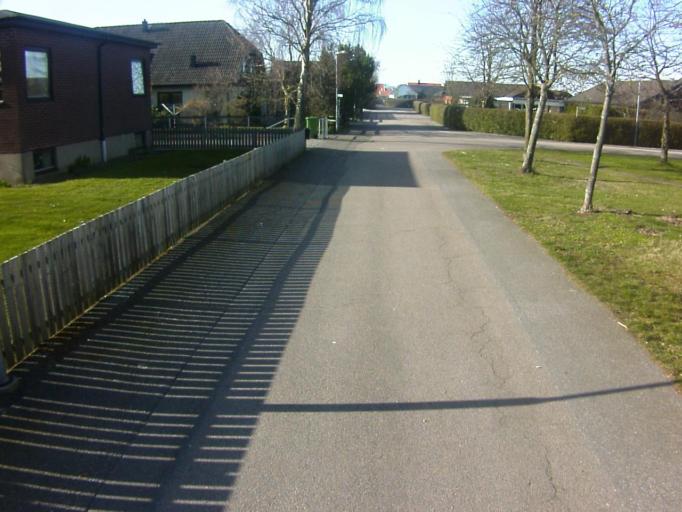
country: SE
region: Skane
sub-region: Kavlinge Kommun
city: Kaevlinge
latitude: 55.8039
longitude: 13.1075
